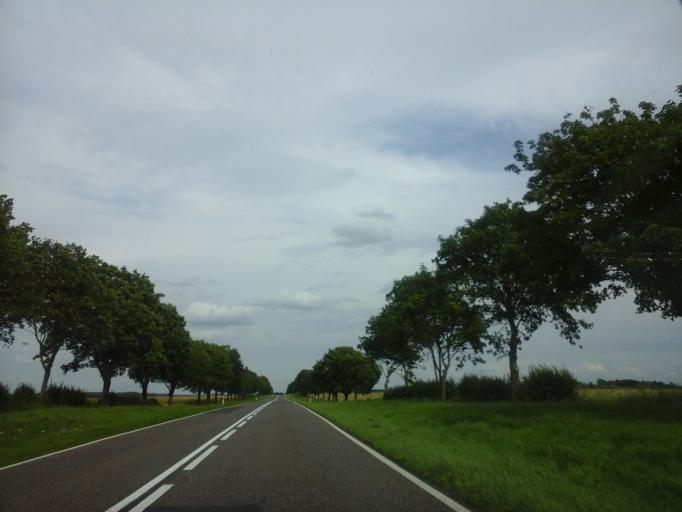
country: PL
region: West Pomeranian Voivodeship
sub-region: Powiat stargardzki
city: Suchan
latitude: 53.2750
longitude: 15.3737
